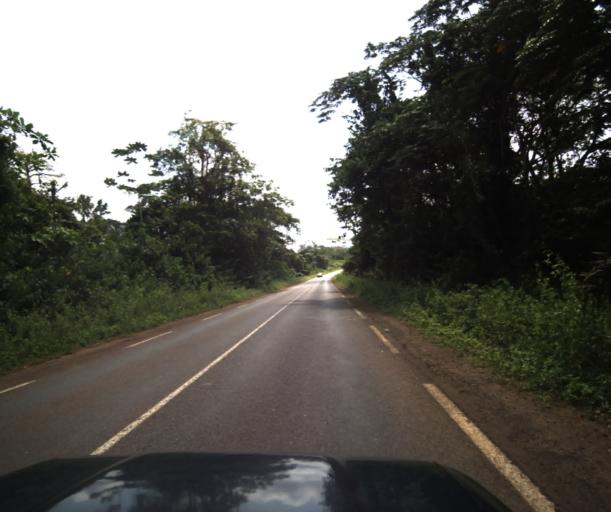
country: CM
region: Centre
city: Eseka
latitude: 3.8903
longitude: 10.7877
